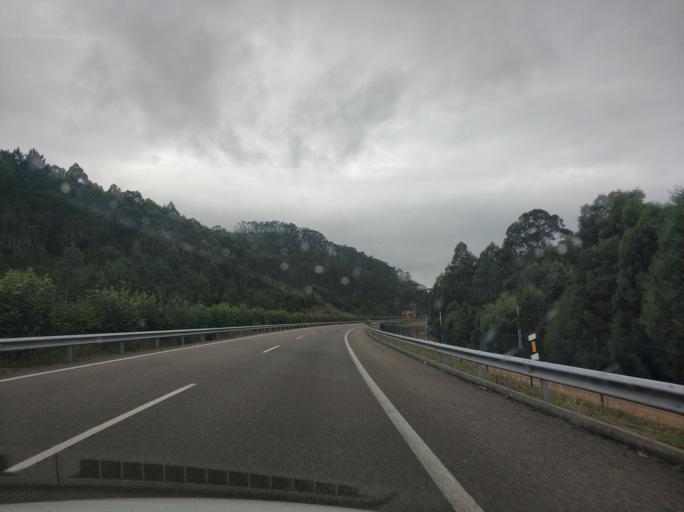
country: ES
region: Galicia
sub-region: Provincia de Lugo
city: Ribadeo
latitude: 43.5348
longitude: -7.1205
